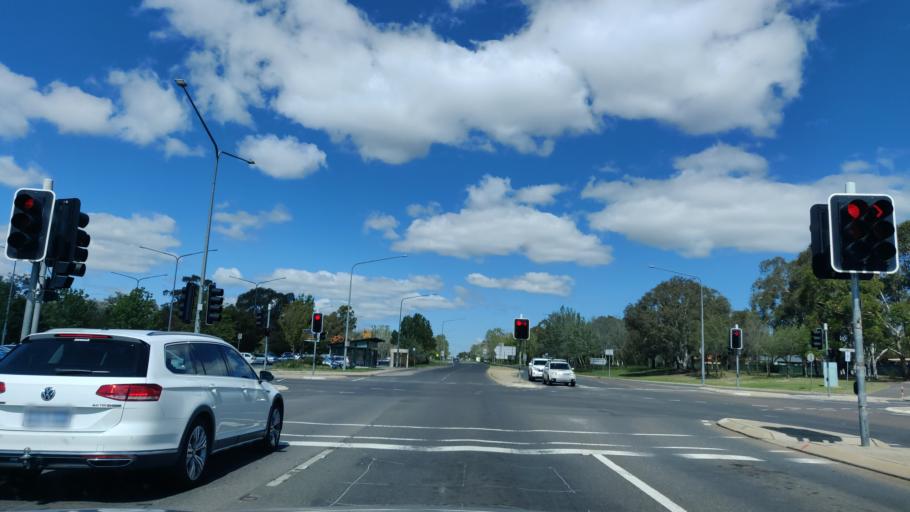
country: AU
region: Australian Capital Territory
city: Macarthur
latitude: -35.3641
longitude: 149.0925
